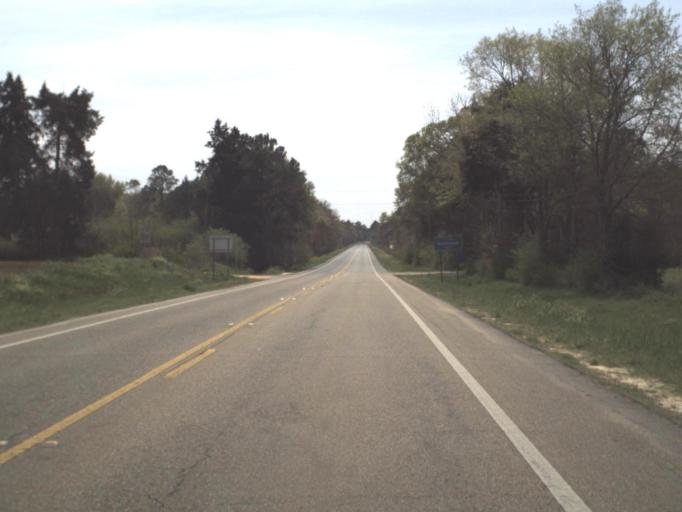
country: US
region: Florida
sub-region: Washington County
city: Chipley
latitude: 30.8310
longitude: -85.5330
